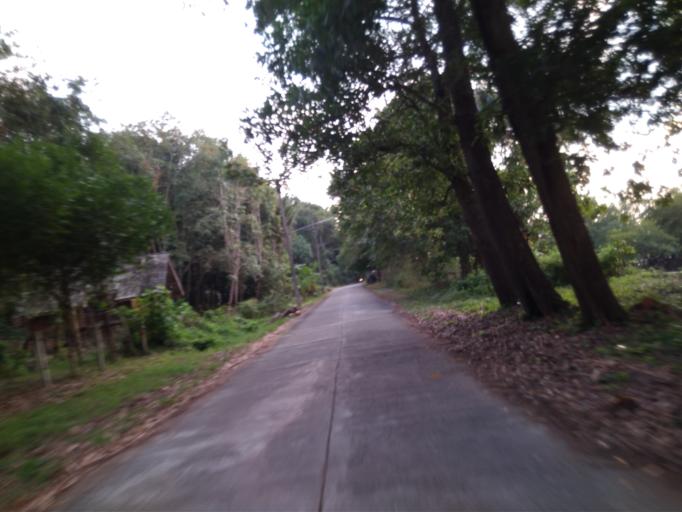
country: TH
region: Phangnga
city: Ko Yao
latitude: 8.1509
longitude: 98.5998
